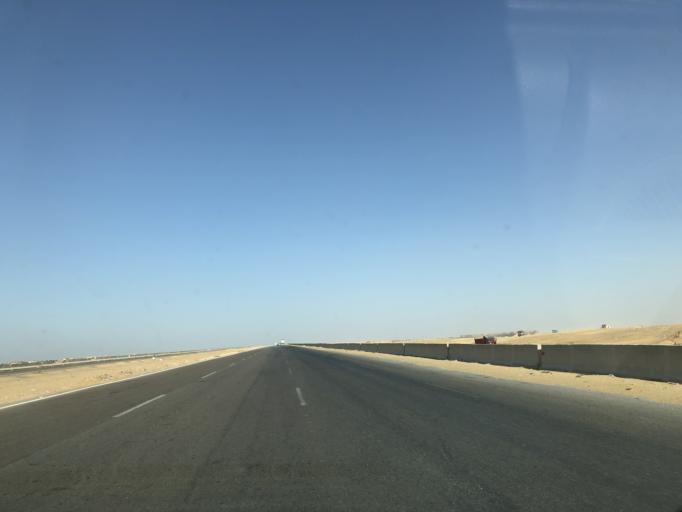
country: EG
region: Muhafazat al Minufiyah
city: Ashmun
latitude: 30.0675
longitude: 30.8609
